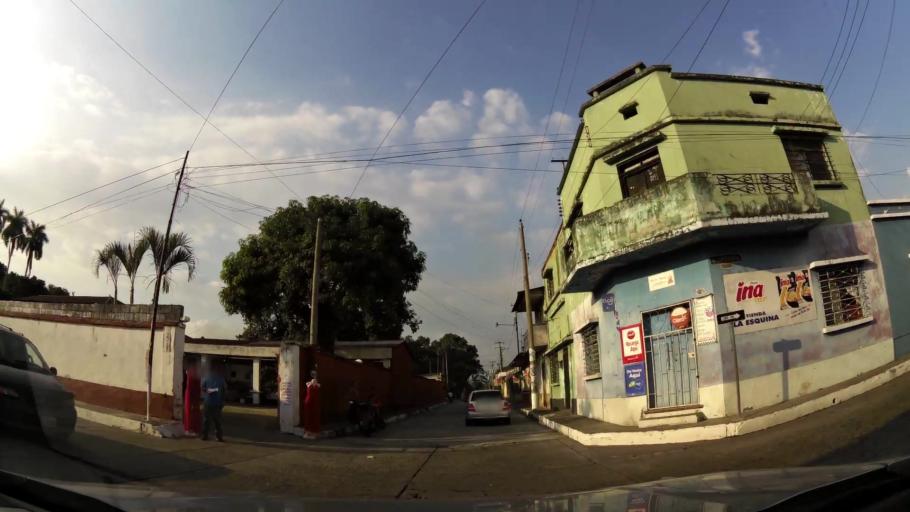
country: GT
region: Retalhuleu
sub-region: Municipio de Retalhuleu
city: Retalhuleu
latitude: 14.5371
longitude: -91.6823
